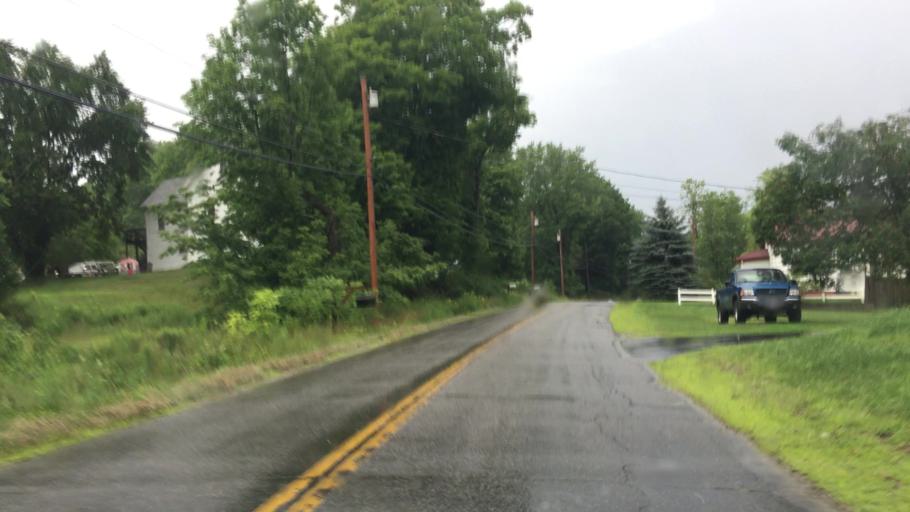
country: US
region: Maine
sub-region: Kennebec County
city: Gardiner
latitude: 44.2118
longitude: -69.8063
